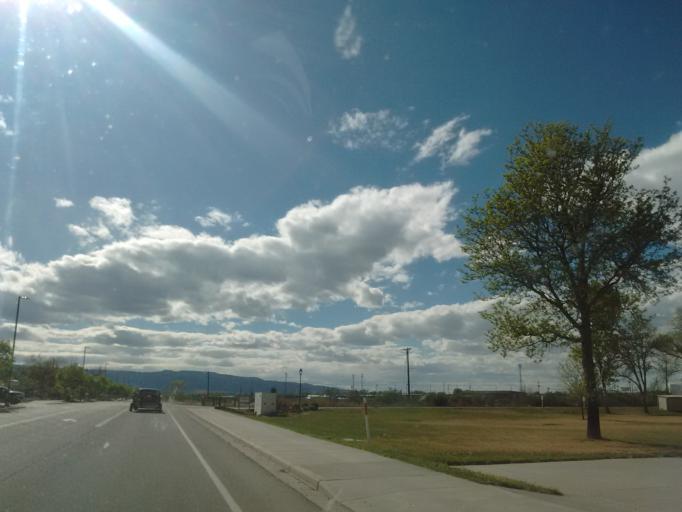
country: US
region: Colorado
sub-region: Mesa County
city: Grand Junction
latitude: 39.0630
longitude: -108.5330
